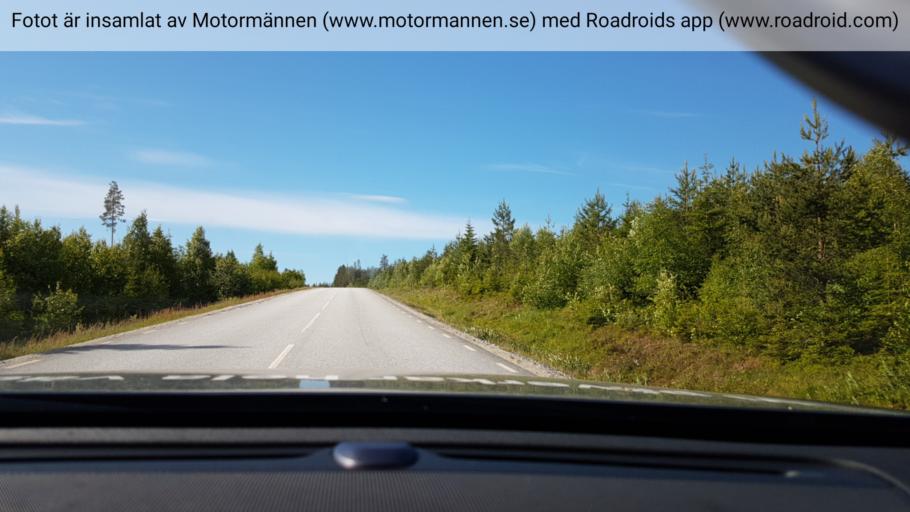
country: SE
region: Vaesterbotten
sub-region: Bjurholms Kommun
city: Bjurholm
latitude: 64.1813
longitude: 19.4021
